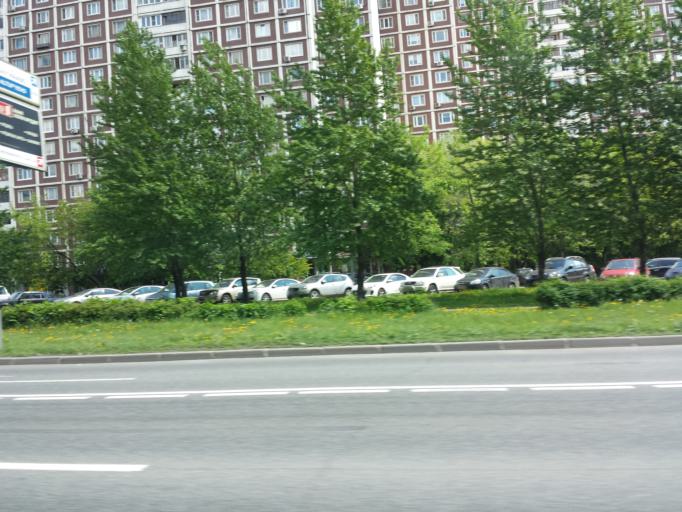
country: RU
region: Moscow
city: Lianozovo
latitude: 55.8951
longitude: 37.5870
